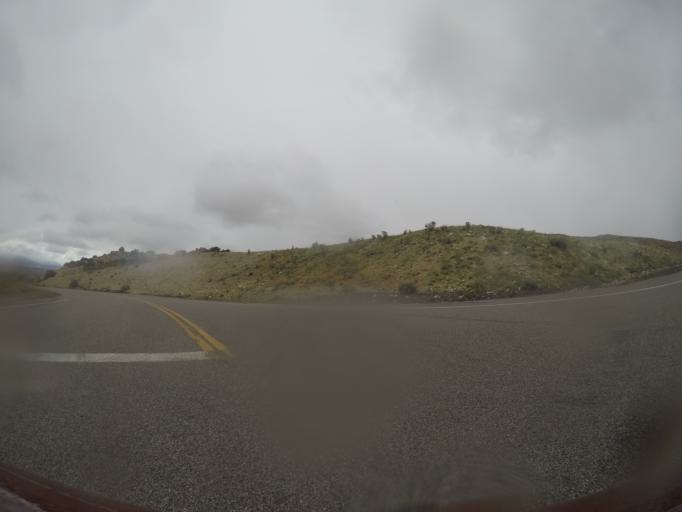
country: US
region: Wyoming
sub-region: Big Horn County
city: Lovell
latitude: 45.0262
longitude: -108.2659
